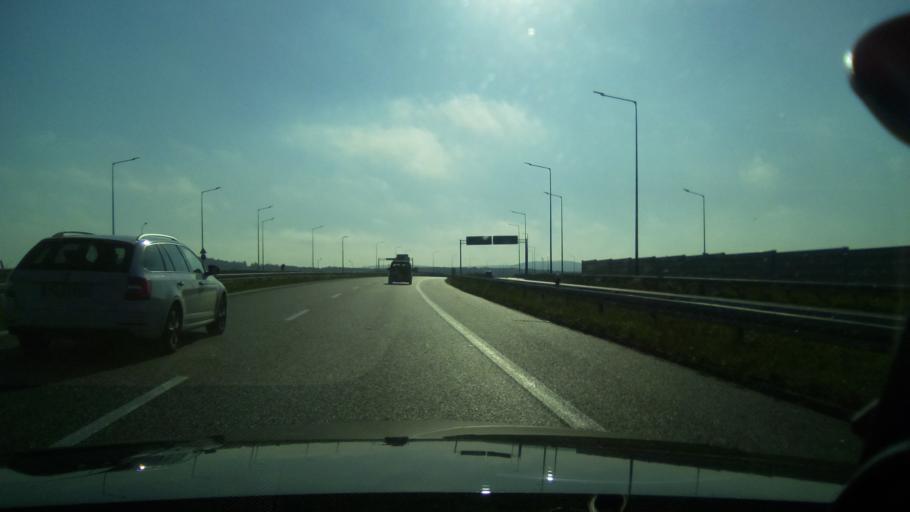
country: PL
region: Silesian Voivodeship
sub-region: Powiat bedzinski
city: Siewierz
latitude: 50.4201
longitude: 19.2076
